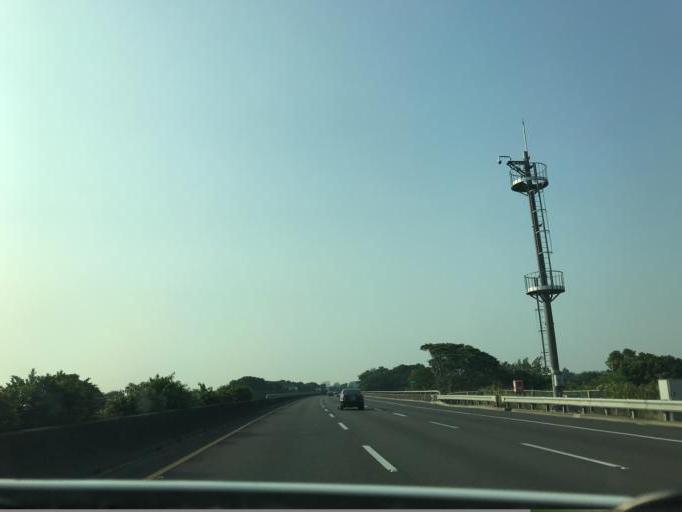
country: TW
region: Taiwan
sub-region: Chiayi
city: Jiayi Shi
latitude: 23.5128
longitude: 120.4035
